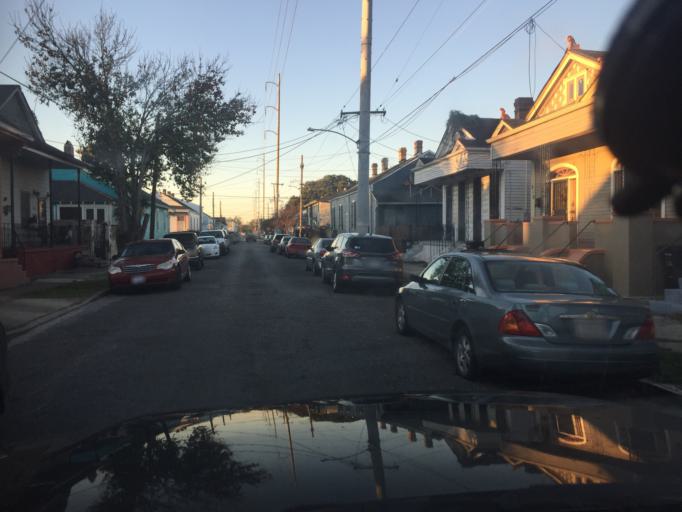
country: US
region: Louisiana
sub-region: Orleans Parish
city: New Orleans
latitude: 29.9739
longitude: -90.0850
